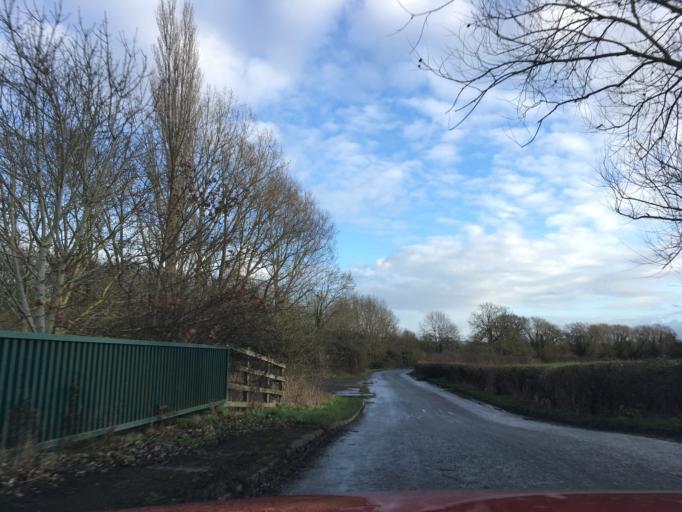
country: GB
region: England
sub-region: Warwickshire
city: Alcester
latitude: 52.2298
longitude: -1.8311
